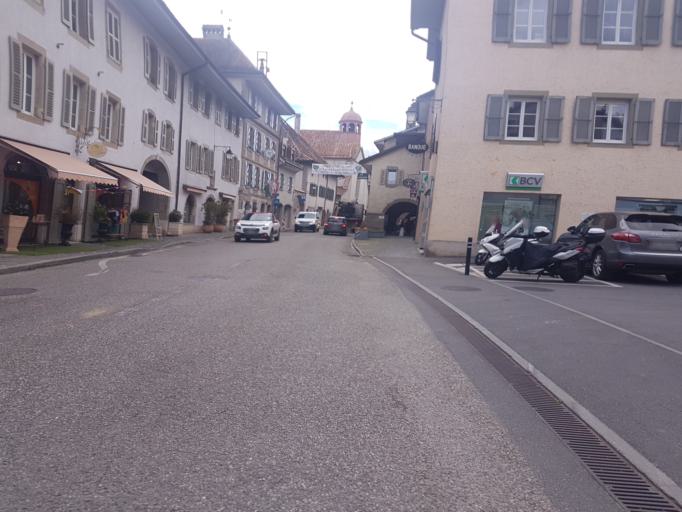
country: CH
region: Vaud
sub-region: Nyon District
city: Coppet
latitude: 46.3168
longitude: 6.1935
